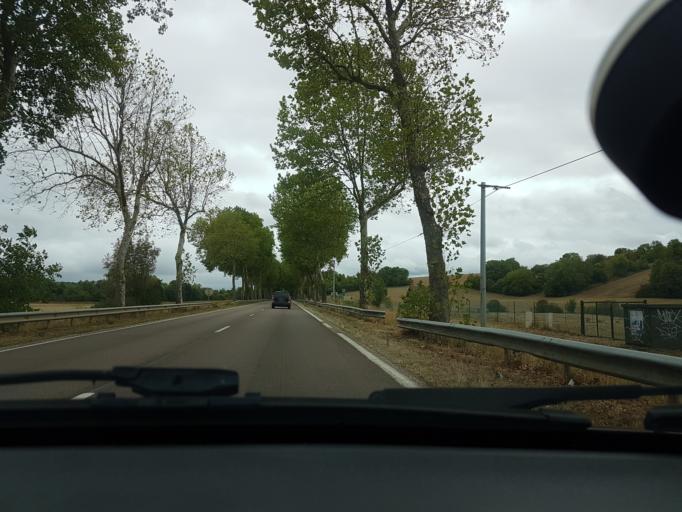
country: FR
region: Bourgogne
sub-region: Departement de l'Yonne
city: Champs-sur-Yonne
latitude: 47.7160
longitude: 3.6173
